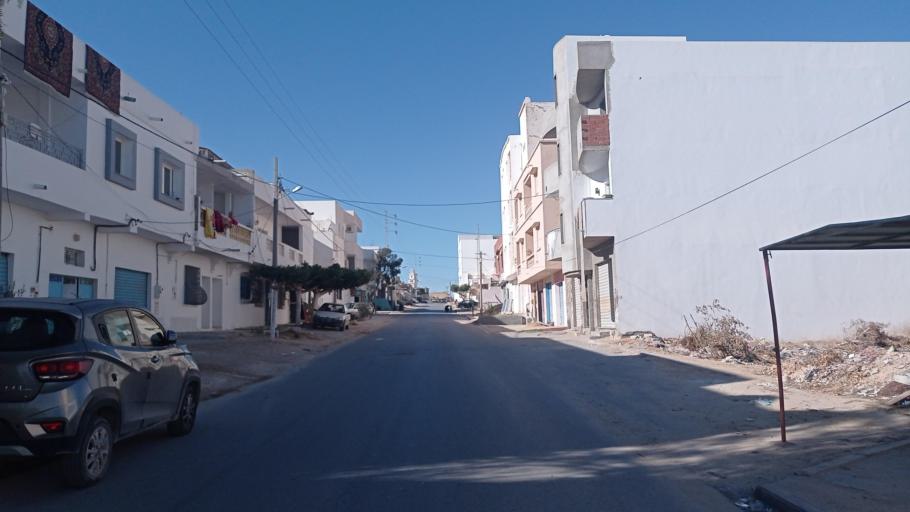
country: TN
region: Qabis
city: Gabes
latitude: 33.8461
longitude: 10.1117
